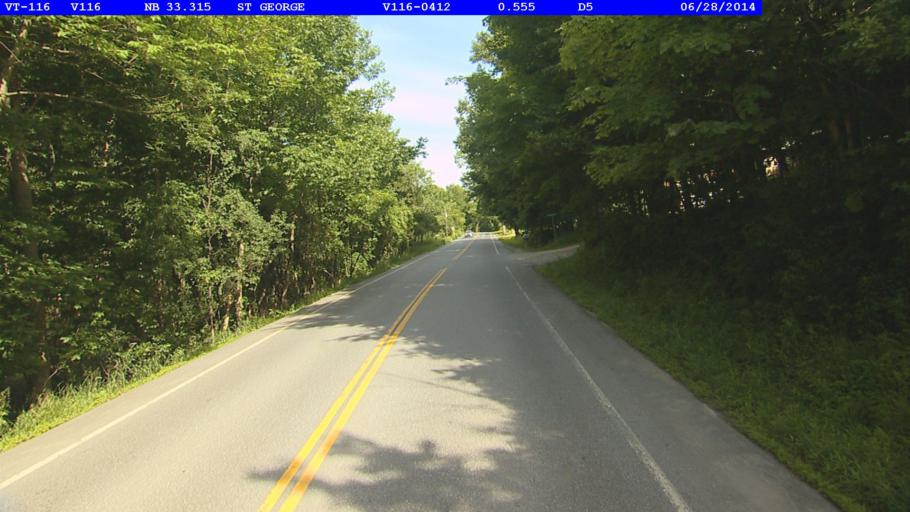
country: US
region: Vermont
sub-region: Chittenden County
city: Hinesburg
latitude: 44.3721
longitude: -73.1316
